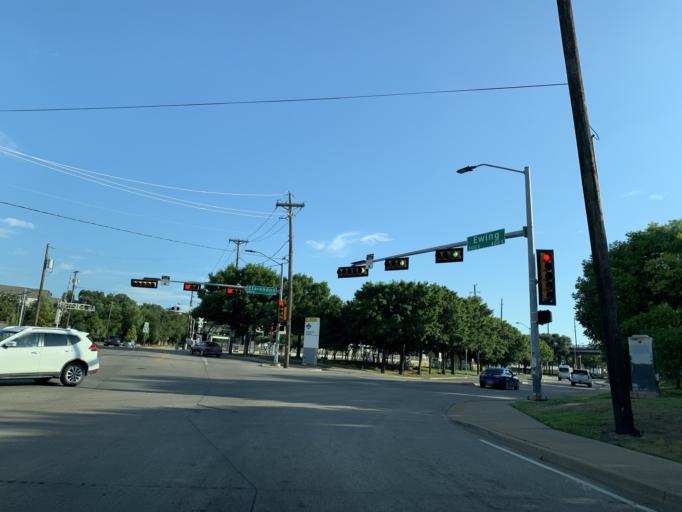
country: US
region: Texas
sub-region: Dallas County
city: Dallas
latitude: 32.7419
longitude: -96.8128
